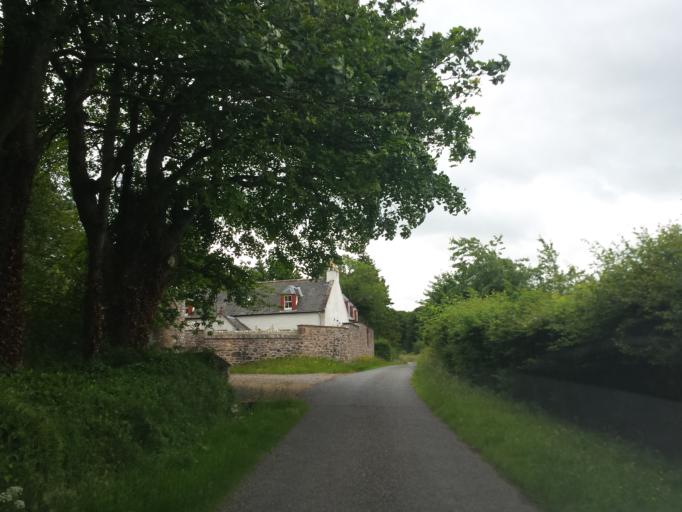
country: GB
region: Scotland
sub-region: Highland
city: Fortrose
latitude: 57.5093
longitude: -4.0416
